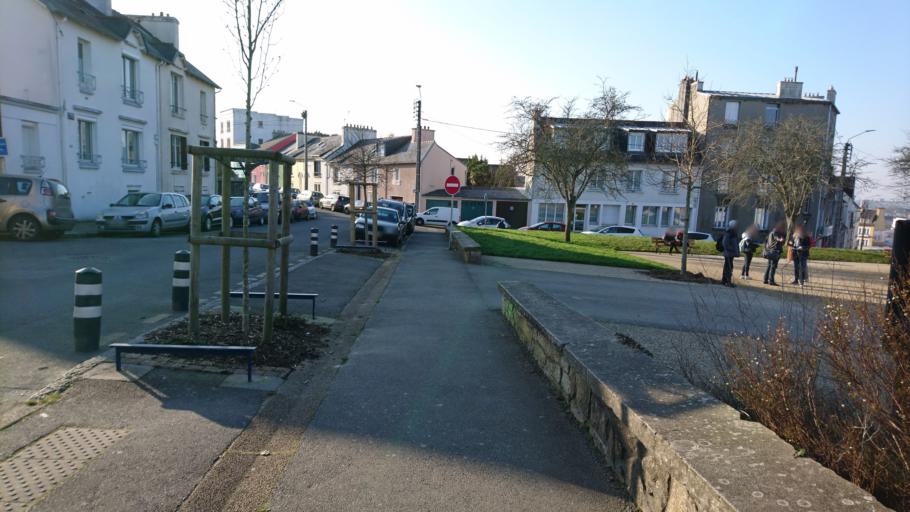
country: FR
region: Brittany
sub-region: Departement du Finistere
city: Brest
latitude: 48.3979
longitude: -4.4857
